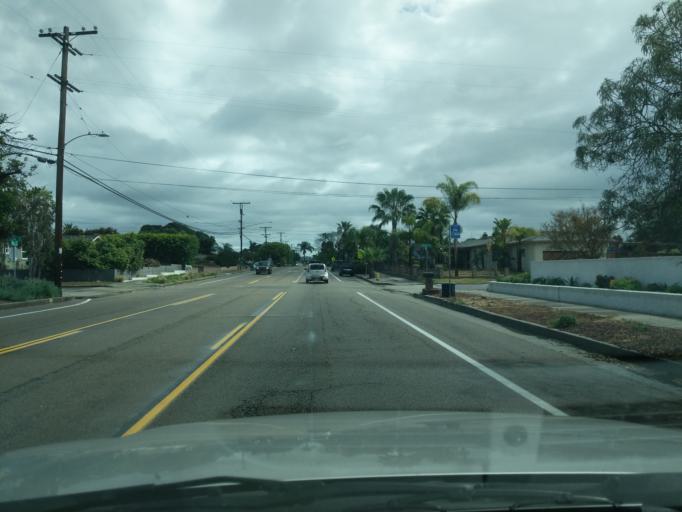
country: US
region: California
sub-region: San Diego County
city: Carlsbad
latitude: 33.1736
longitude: -117.3569
